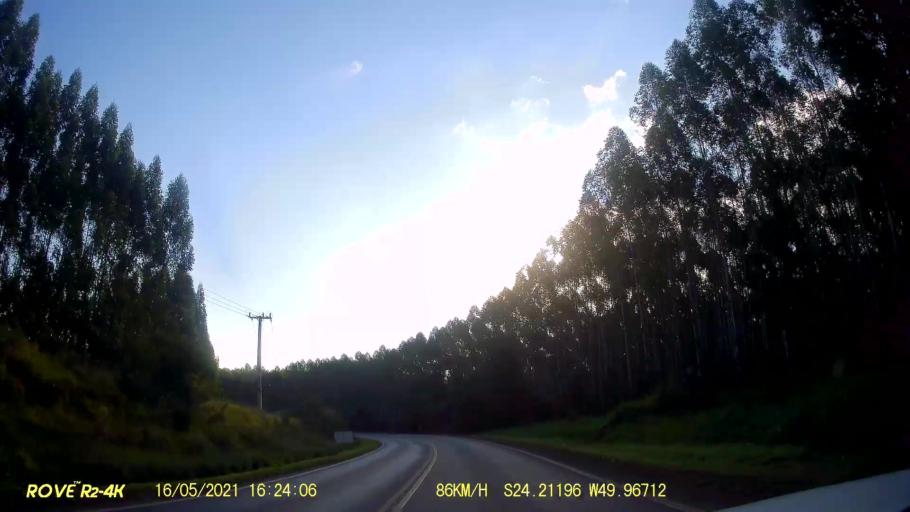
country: BR
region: Parana
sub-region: Jaguariaiva
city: Jaguariaiva
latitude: -24.2120
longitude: -49.9673
